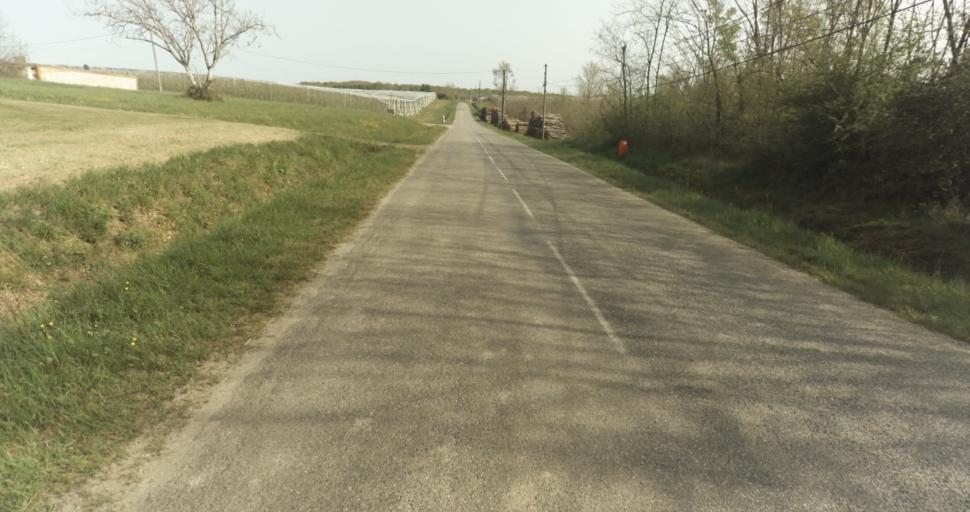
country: FR
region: Midi-Pyrenees
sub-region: Departement du Tarn-et-Garonne
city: Moissac
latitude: 44.1494
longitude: 1.0635
